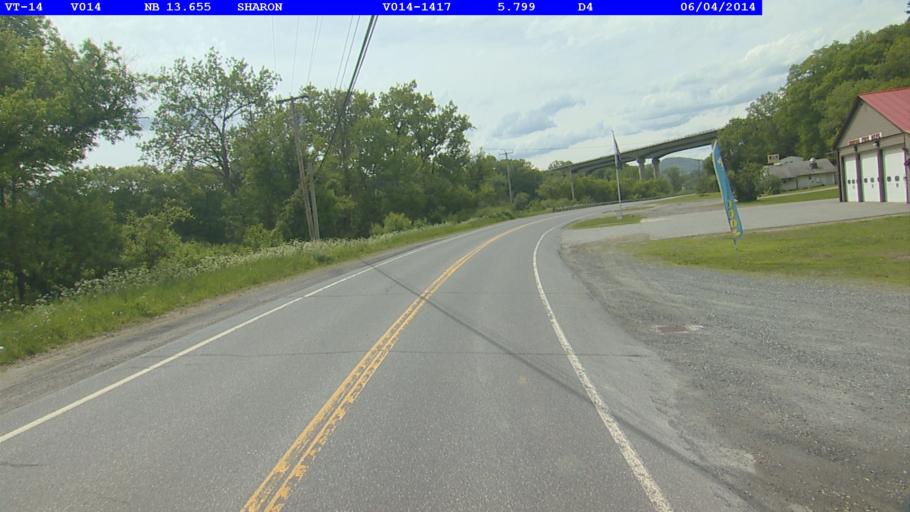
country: US
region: Vermont
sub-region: Windsor County
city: Woodstock
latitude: 43.7807
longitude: -72.4683
